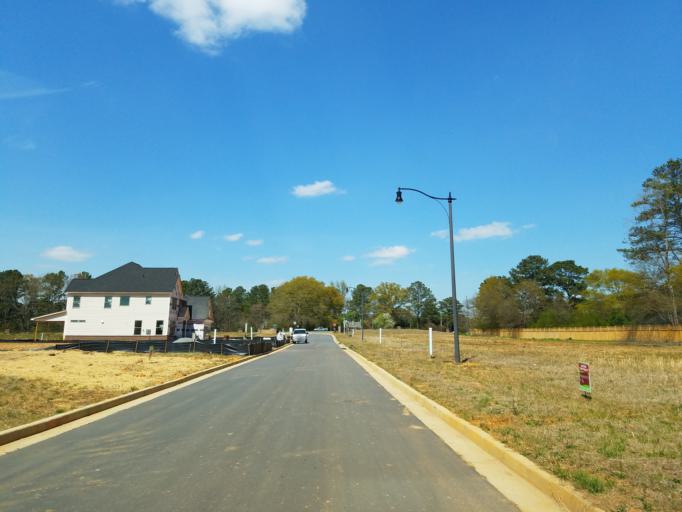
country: US
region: Georgia
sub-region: Cobb County
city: Powder Springs
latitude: 33.9004
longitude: -84.6211
